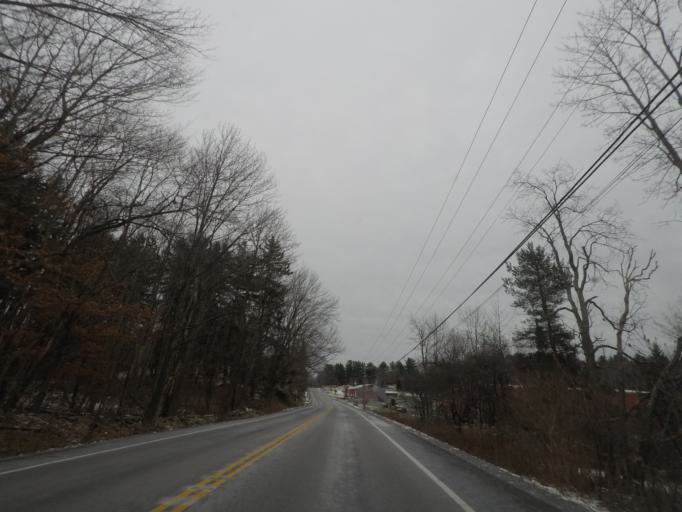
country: US
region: New York
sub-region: Rensselaer County
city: Hoosick Falls
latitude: 42.7692
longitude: -73.4199
